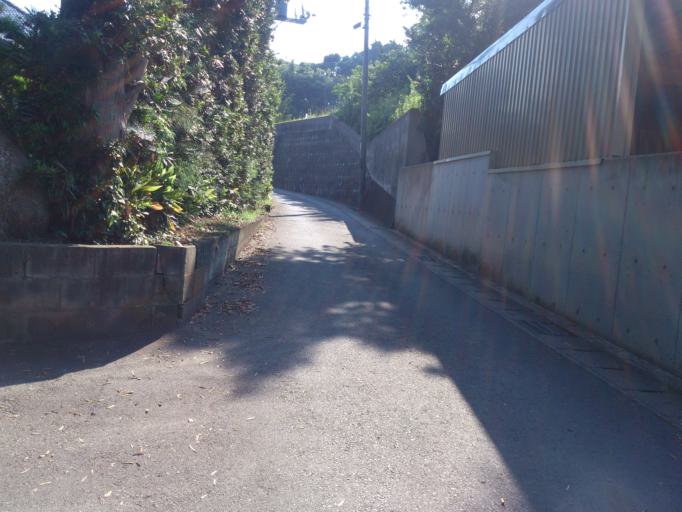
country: JP
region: Chiba
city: Tateyama
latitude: 35.0626
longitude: 139.8294
